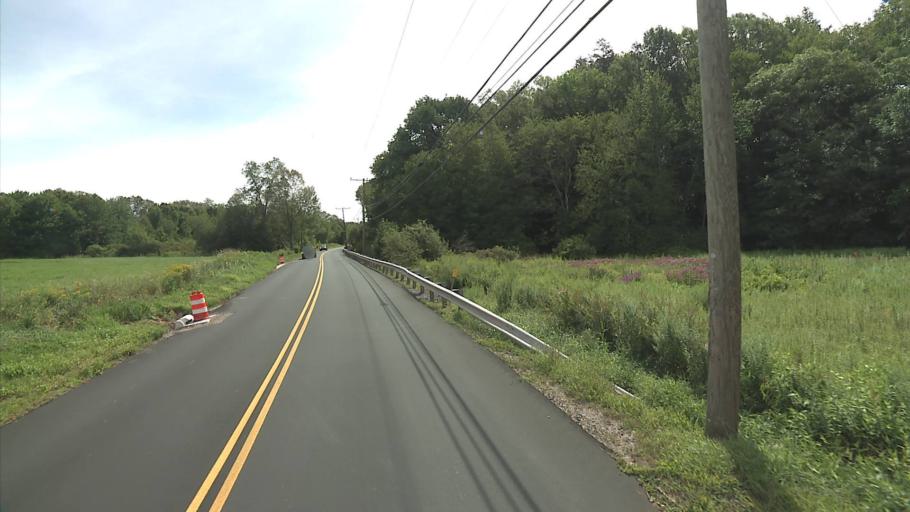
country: US
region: Connecticut
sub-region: Windham County
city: South Woodstock
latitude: 41.9380
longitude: -71.9892
